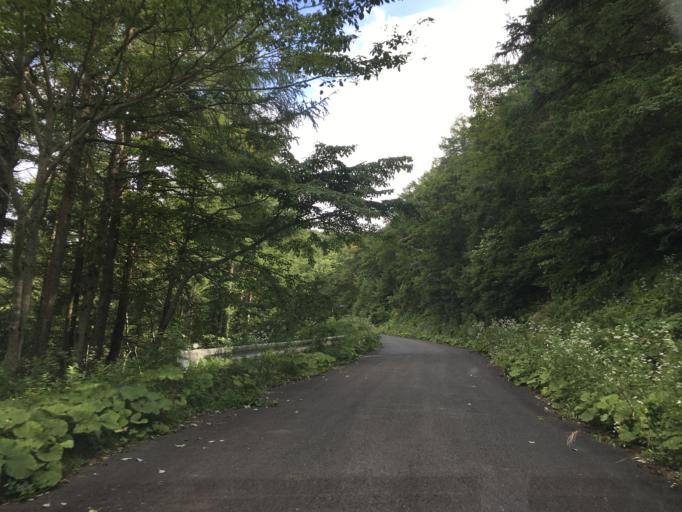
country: JP
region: Iwate
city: Ofunato
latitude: 38.9780
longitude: 141.4520
